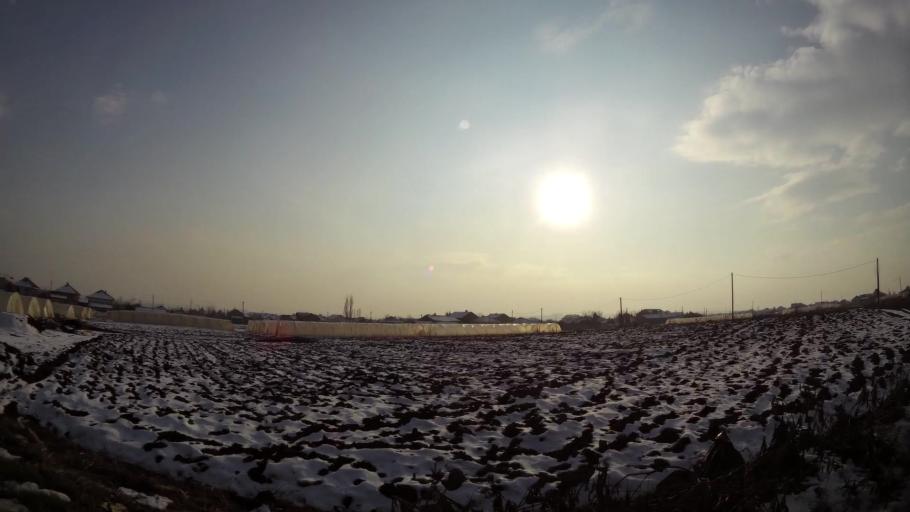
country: MK
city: Creshevo
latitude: 42.0327
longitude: 21.5249
